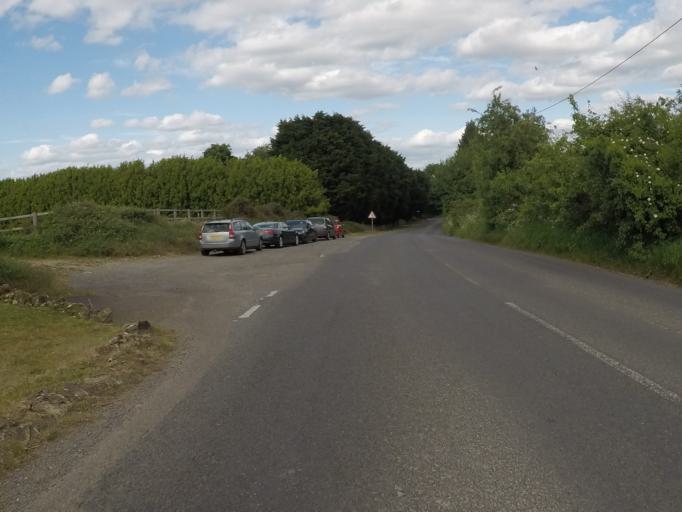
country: GB
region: England
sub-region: Oxfordshire
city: Charlbury
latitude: 51.8468
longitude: -1.4792
